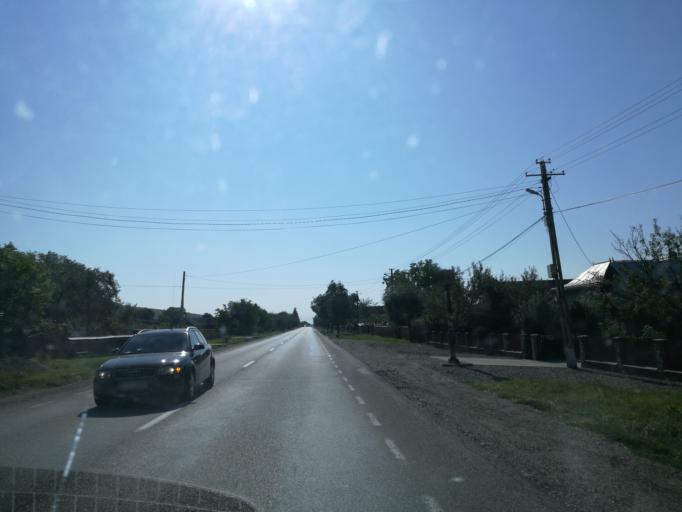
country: RO
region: Neamt
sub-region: Comuna Draganesti
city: Draganesti
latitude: 47.3534
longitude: 26.4082
